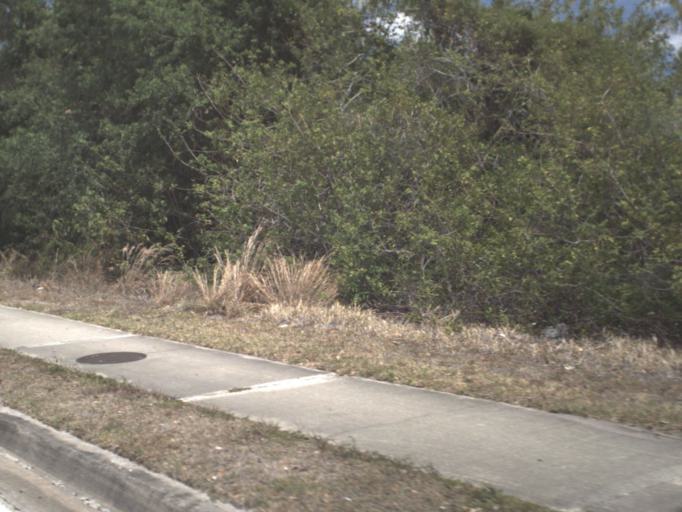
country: US
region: Florida
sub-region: Brevard County
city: Palm Bay
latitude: 28.0427
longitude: -80.6215
